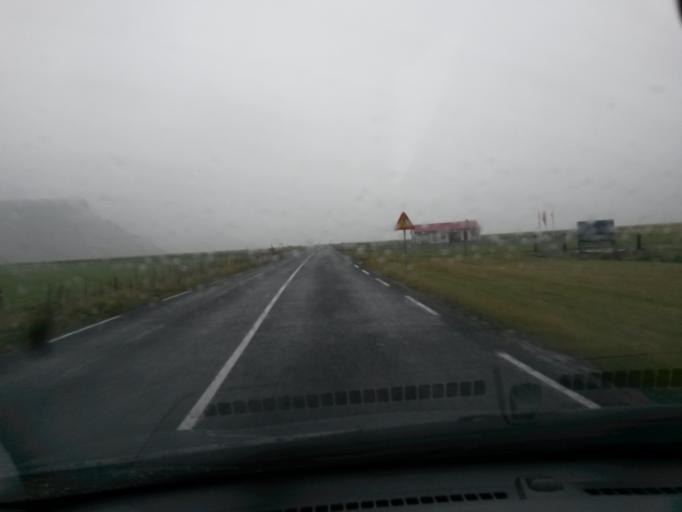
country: IS
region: South
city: Vestmannaeyjar
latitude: 63.5434
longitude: -19.6704
